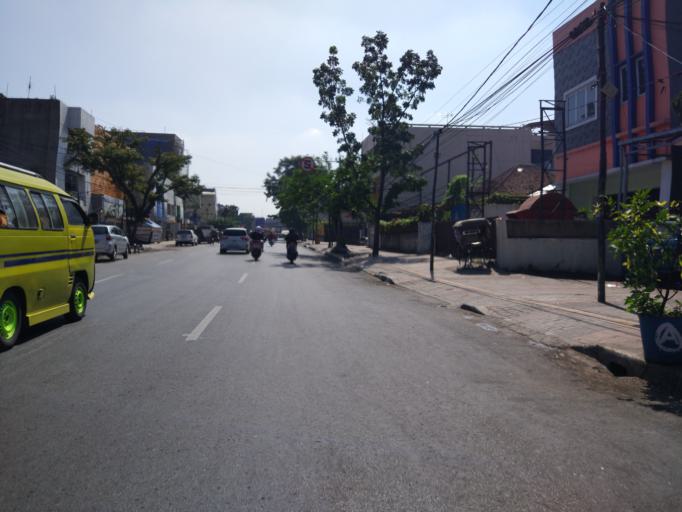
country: ID
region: West Java
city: Bandung
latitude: -6.9288
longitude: 107.5977
